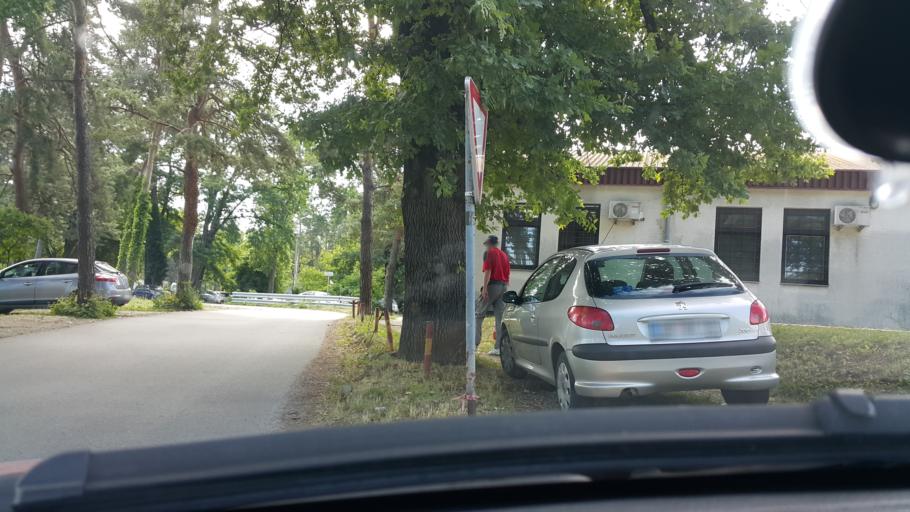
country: SI
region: Hoce-Slivnica
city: Rogoza
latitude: 46.5287
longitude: 15.6681
